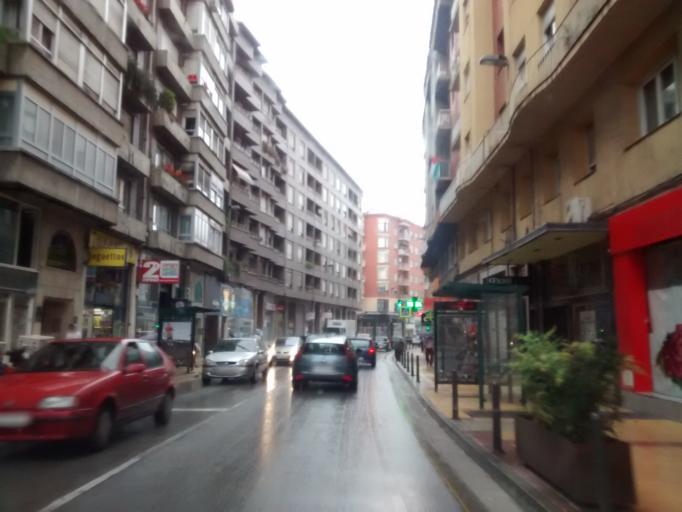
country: ES
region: Cantabria
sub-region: Provincia de Cantabria
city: Torrelavega
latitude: 43.3521
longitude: -4.0491
